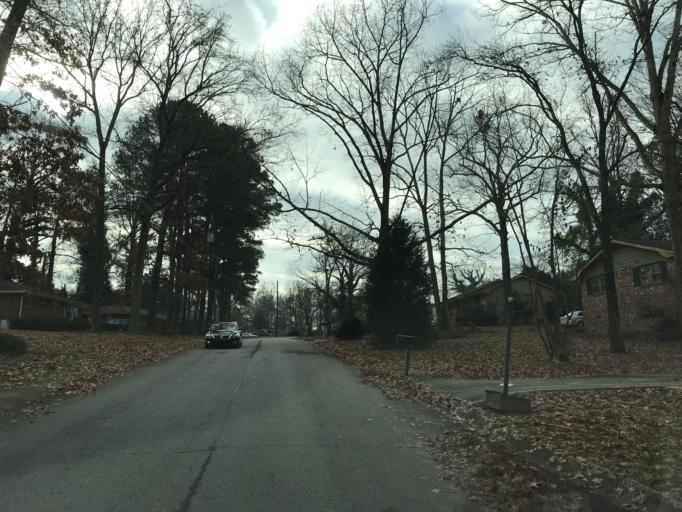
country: US
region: Georgia
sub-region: Clayton County
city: Riverdale
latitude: 33.5713
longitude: -84.3755
